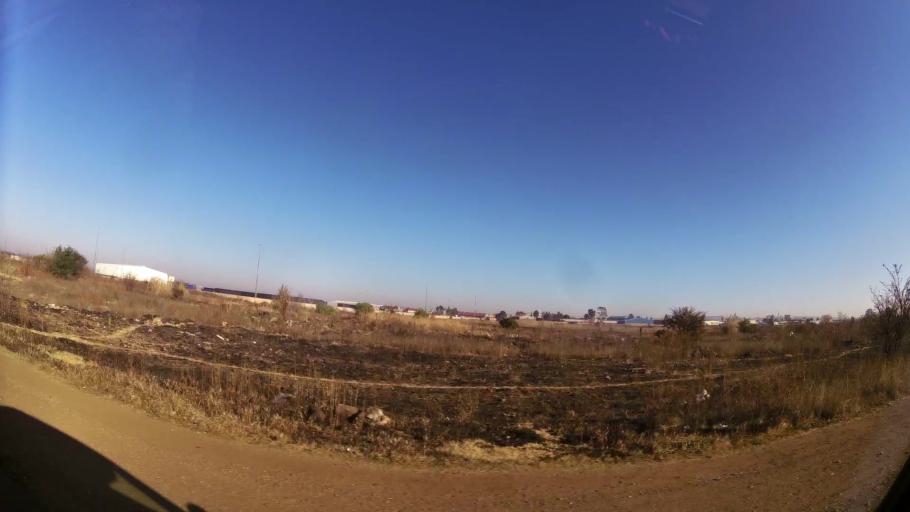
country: ZA
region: Gauteng
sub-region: Ekurhuleni Metropolitan Municipality
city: Germiston
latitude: -26.3293
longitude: 28.1380
